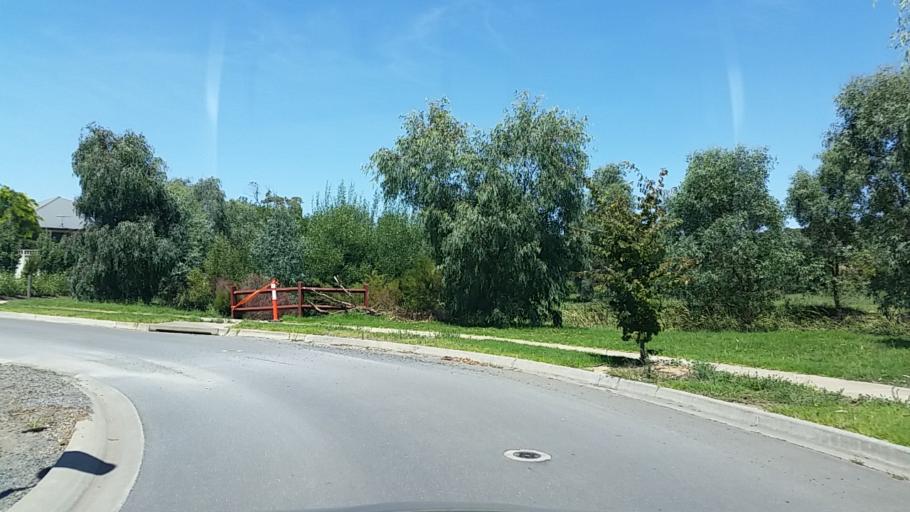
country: AU
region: South Australia
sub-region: Mount Barker
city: Little Hampton
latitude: -35.0403
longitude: 138.8646
